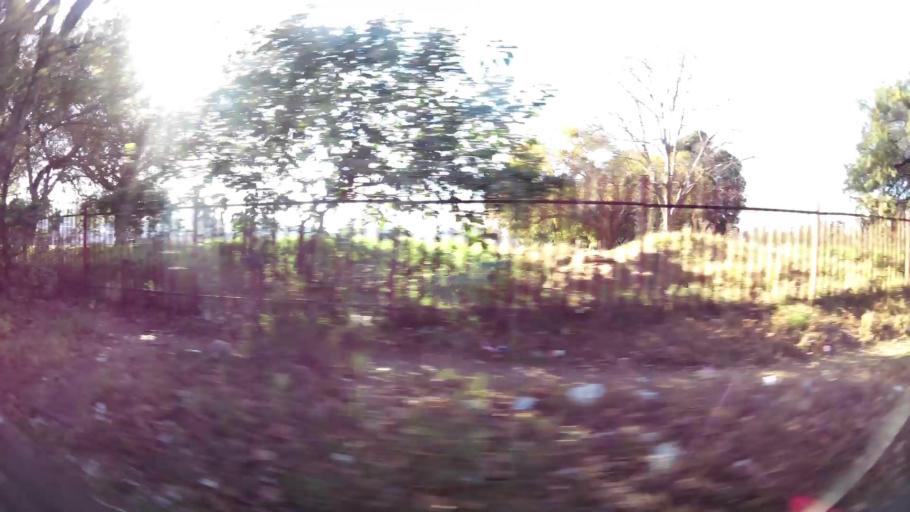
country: ZA
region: Gauteng
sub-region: City of Johannesburg Metropolitan Municipality
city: Johannesburg
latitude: -26.2049
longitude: 27.9904
